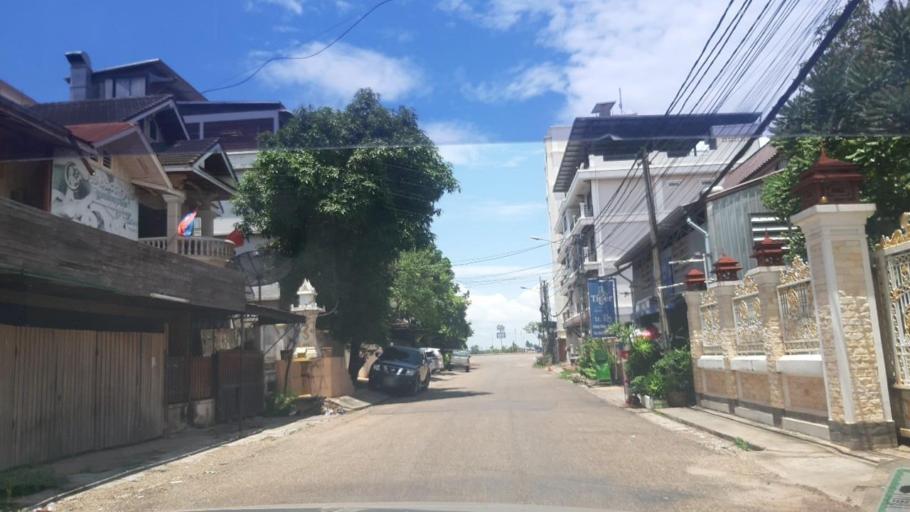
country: LA
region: Vientiane
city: Vientiane
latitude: 17.9674
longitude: 102.5933
